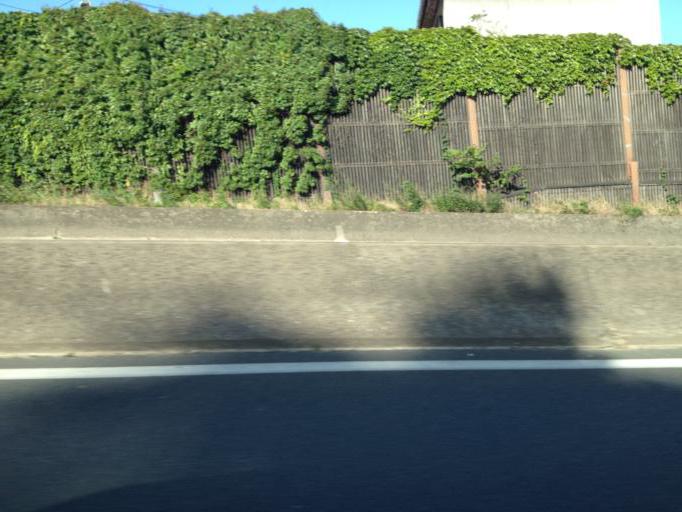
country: FR
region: Ile-de-France
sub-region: Departement de l'Essonne
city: Orsay
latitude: 48.7058
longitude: 2.1920
